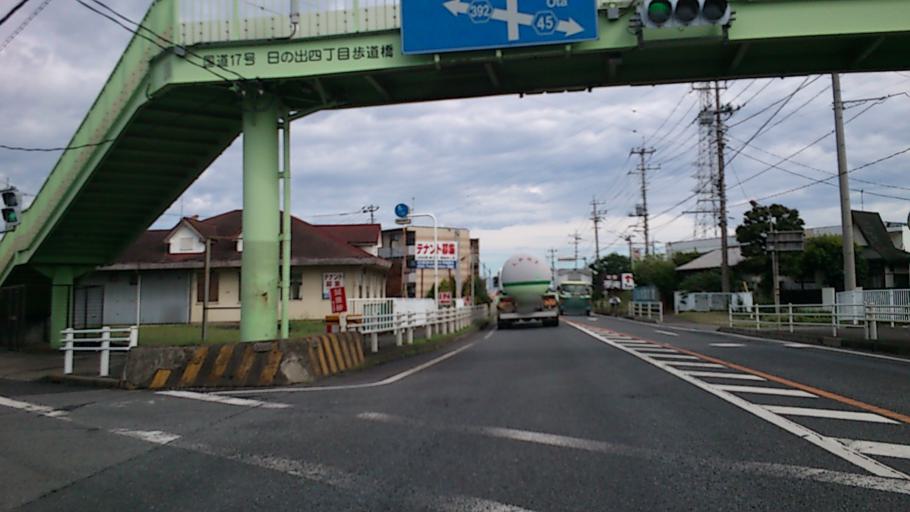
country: JP
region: Saitama
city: Honjo
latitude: 36.2365
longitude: 139.2072
